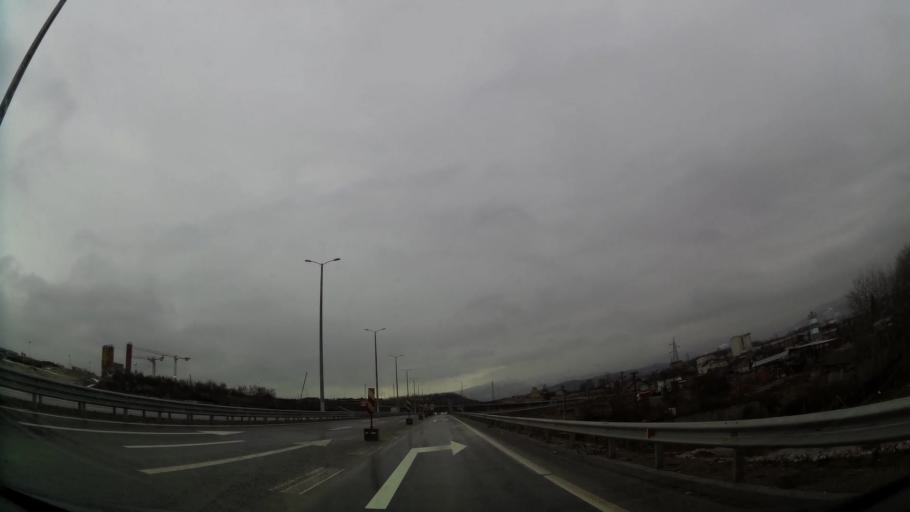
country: XK
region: Ferizaj
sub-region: Komuna e Kacanikut
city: Kacanik
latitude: 42.2792
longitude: 21.2111
